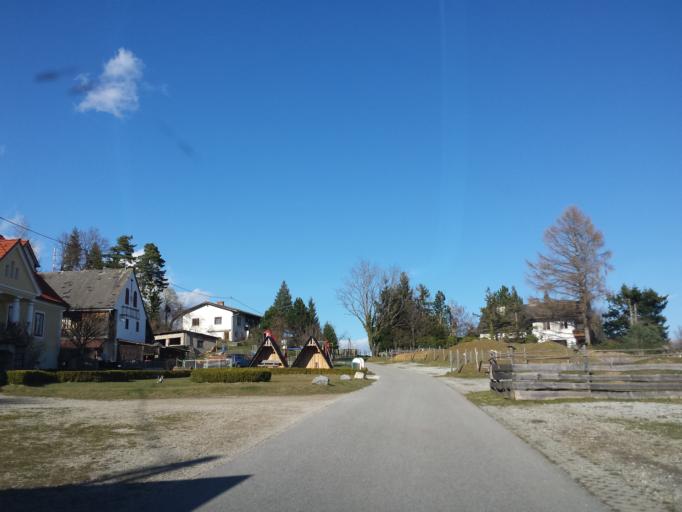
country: AT
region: Styria
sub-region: Politischer Bezirk Graz-Umgebung
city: Sankt Radegund bei Graz
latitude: 47.1681
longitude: 15.4780
